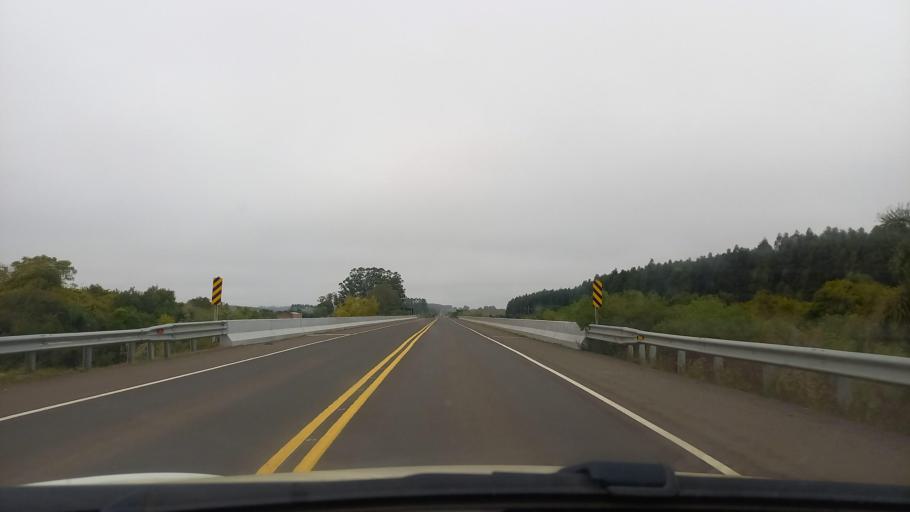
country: BR
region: Rio Grande do Sul
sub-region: Rosario Do Sul
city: Rosario do Sul
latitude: -30.2937
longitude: -54.9876
